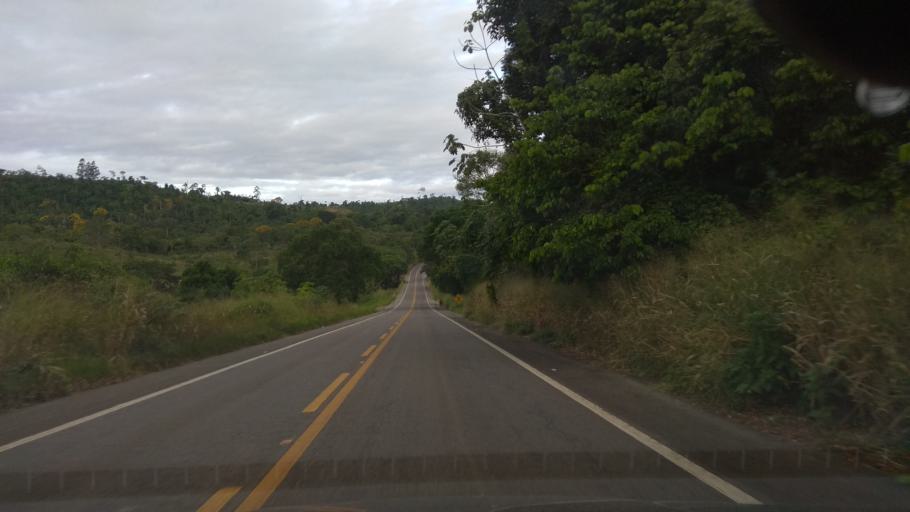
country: BR
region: Bahia
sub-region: Ibirapitanga
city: Ibirapitanga
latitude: -14.2464
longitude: -39.3788
